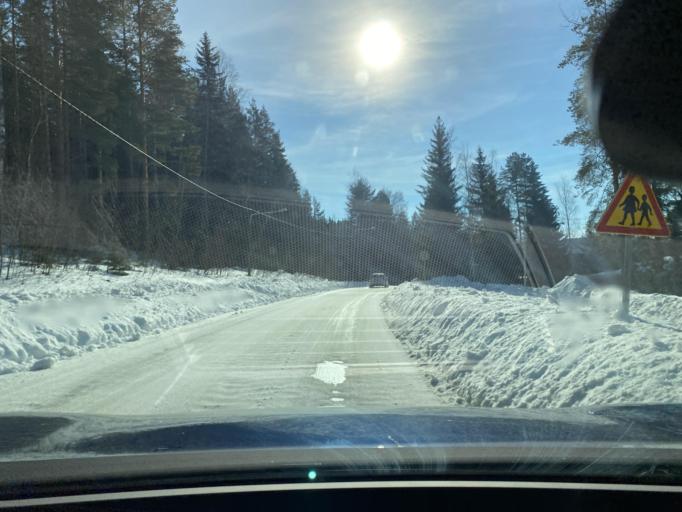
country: FI
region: Central Finland
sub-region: Jyvaeskylae
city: Muurame
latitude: 62.0959
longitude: 25.6440
